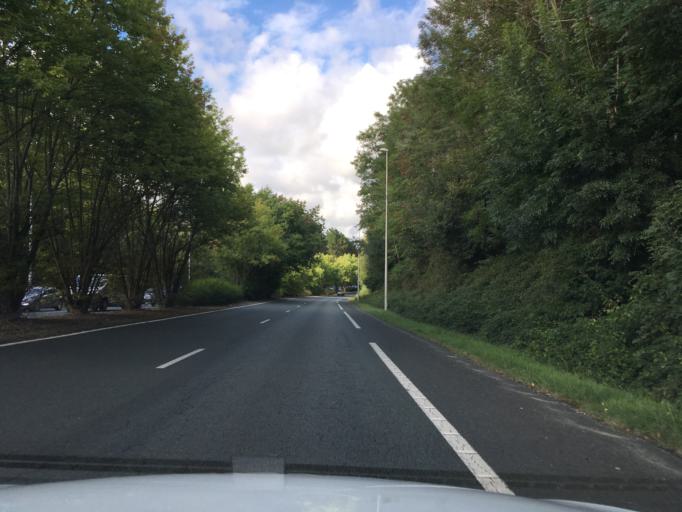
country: FR
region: Aquitaine
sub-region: Departement des Pyrenees-Atlantiques
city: Bayonne
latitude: 43.4689
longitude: -1.4933
